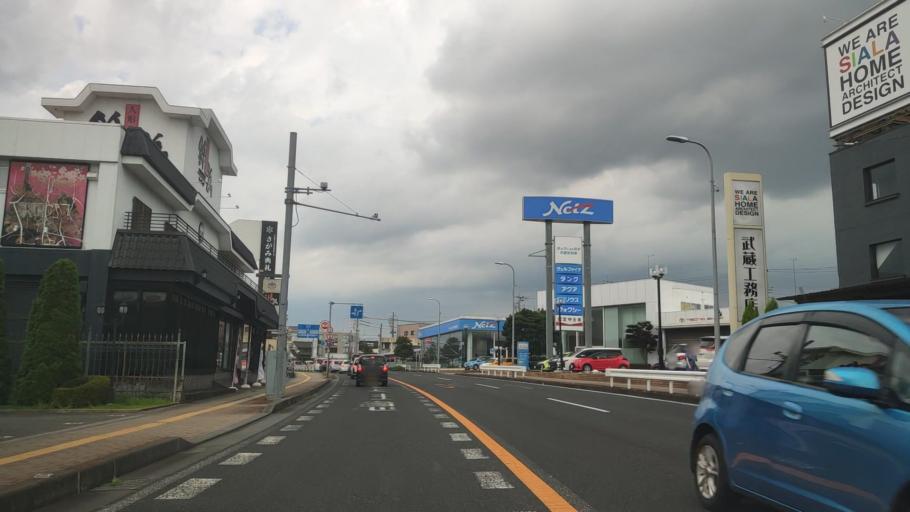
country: JP
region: Tochigi
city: Utsunomiya-shi
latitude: 36.5616
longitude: 139.9153
